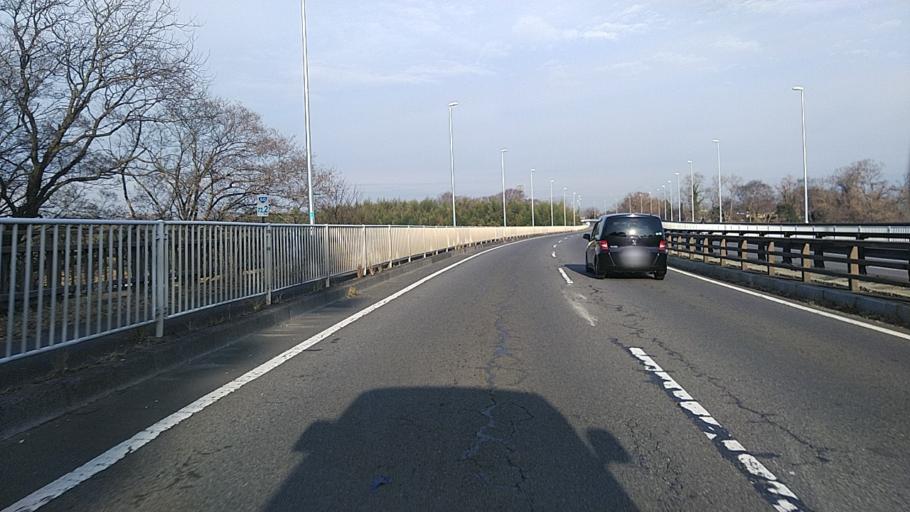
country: JP
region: Tochigi
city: Oyama
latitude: 36.3063
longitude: 139.7874
